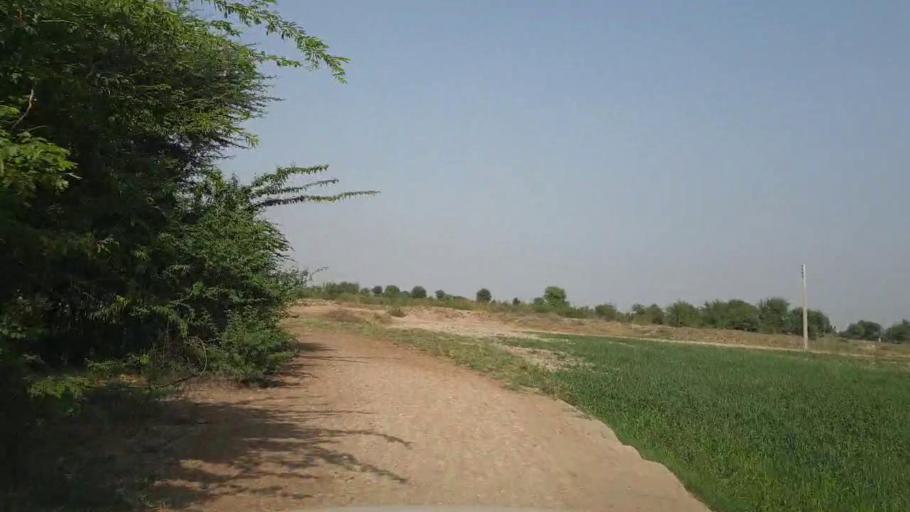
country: PK
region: Sindh
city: Dhoro Naro
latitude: 25.4862
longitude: 69.6102
